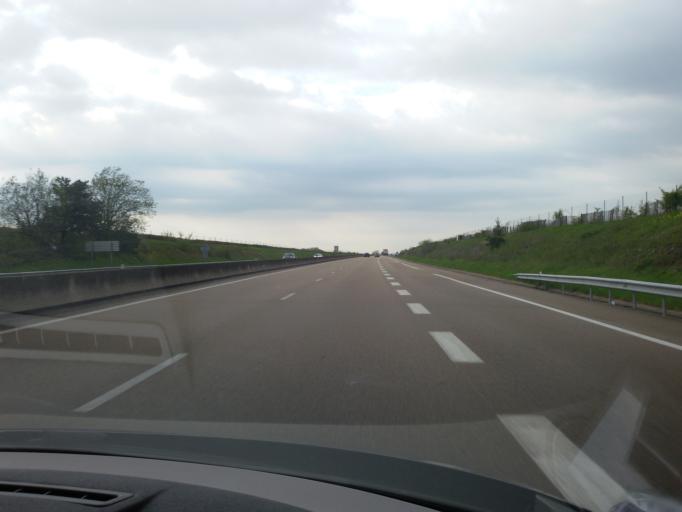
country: FR
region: Champagne-Ardenne
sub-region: Departement de la Haute-Marne
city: Chamarandes-Choignes
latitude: 47.9662
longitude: 5.1459
